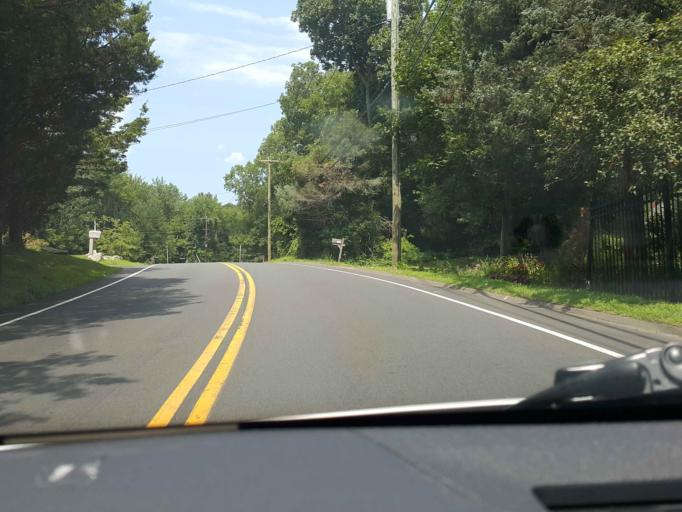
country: US
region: Connecticut
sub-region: New Haven County
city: Guilford
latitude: 41.3016
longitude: -72.6872
